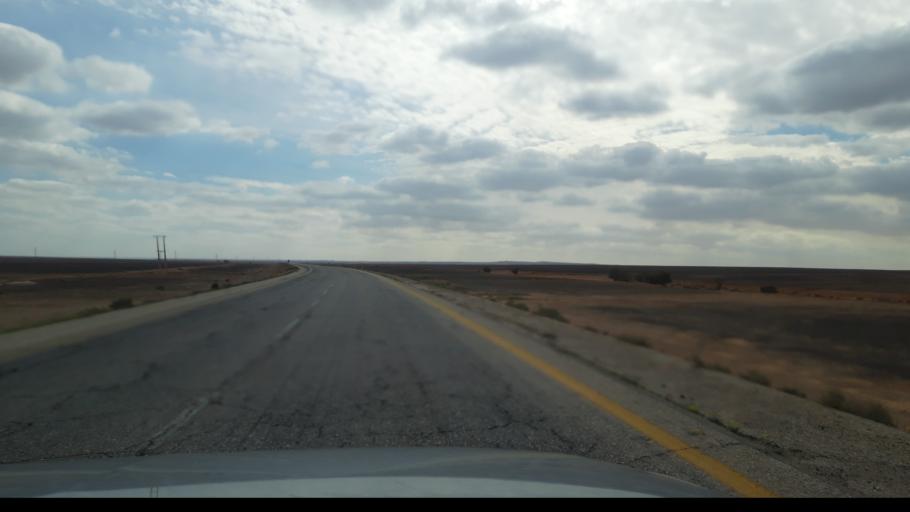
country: JO
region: Amman
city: Al Azraq ash Shamali
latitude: 31.8163
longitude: 36.5995
